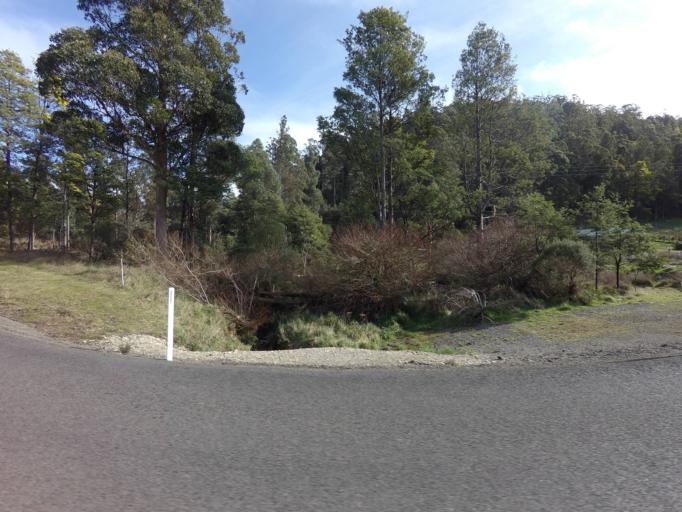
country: AU
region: Tasmania
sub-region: Huon Valley
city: Huonville
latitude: -43.0416
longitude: 147.1326
